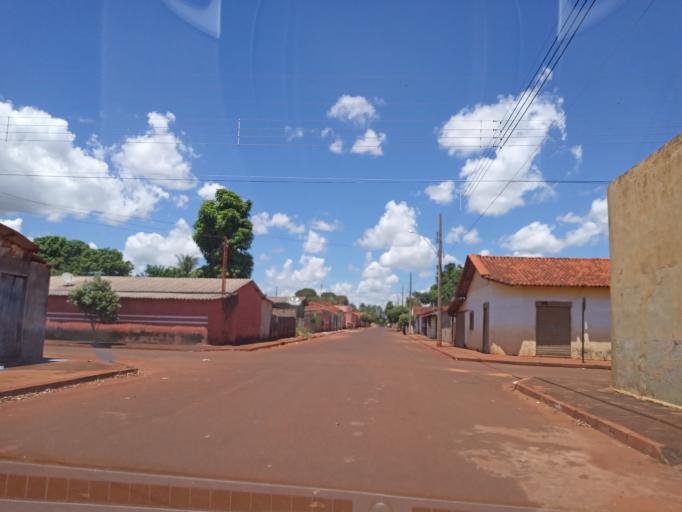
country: BR
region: Minas Gerais
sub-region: Centralina
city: Centralina
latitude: -18.5839
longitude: -49.2048
